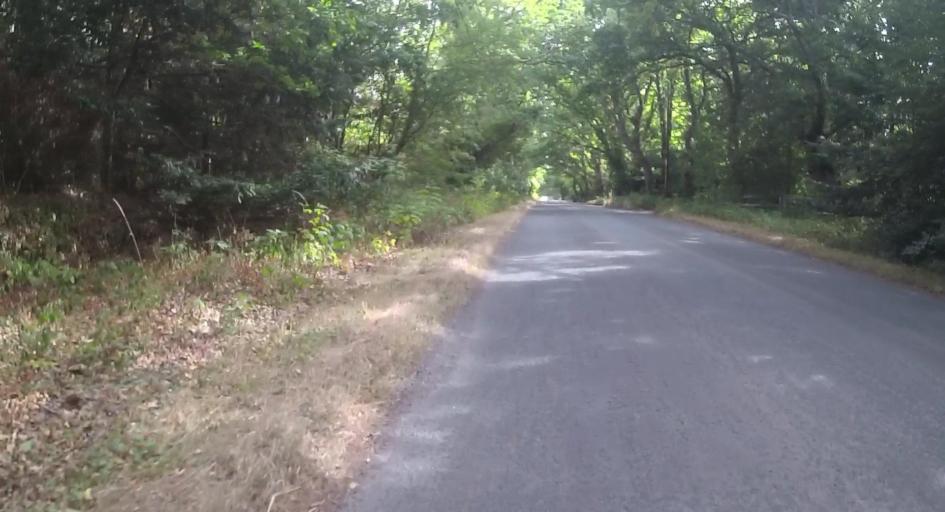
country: GB
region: England
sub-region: Dorset
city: Wareham
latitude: 50.6648
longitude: -2.1149
